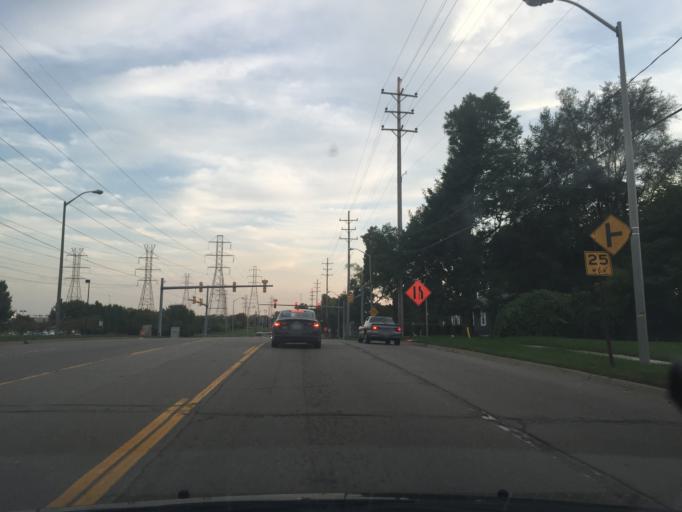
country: US
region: Michigan
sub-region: Oakland County
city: Pontiac
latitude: 42.6235
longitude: -83.2684
